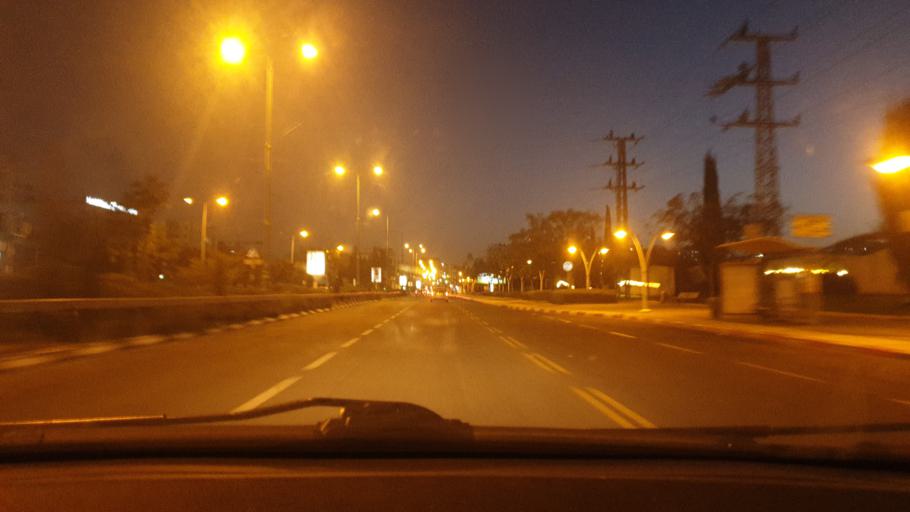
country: IL
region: Central District
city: Rishon LeZiyyon
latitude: 31.9756
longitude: 34.8074
